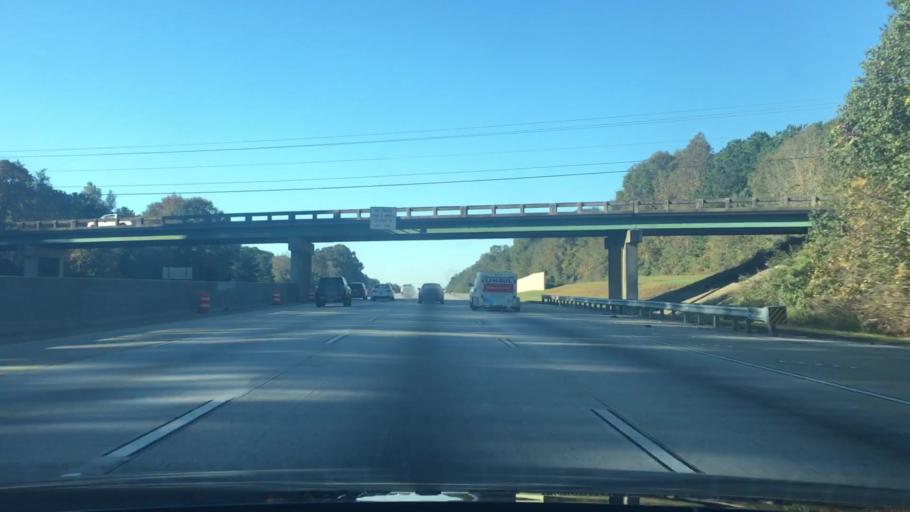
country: US
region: Georgia
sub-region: Fulton County
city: Palmetto
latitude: 33.4817
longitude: -84.6568
